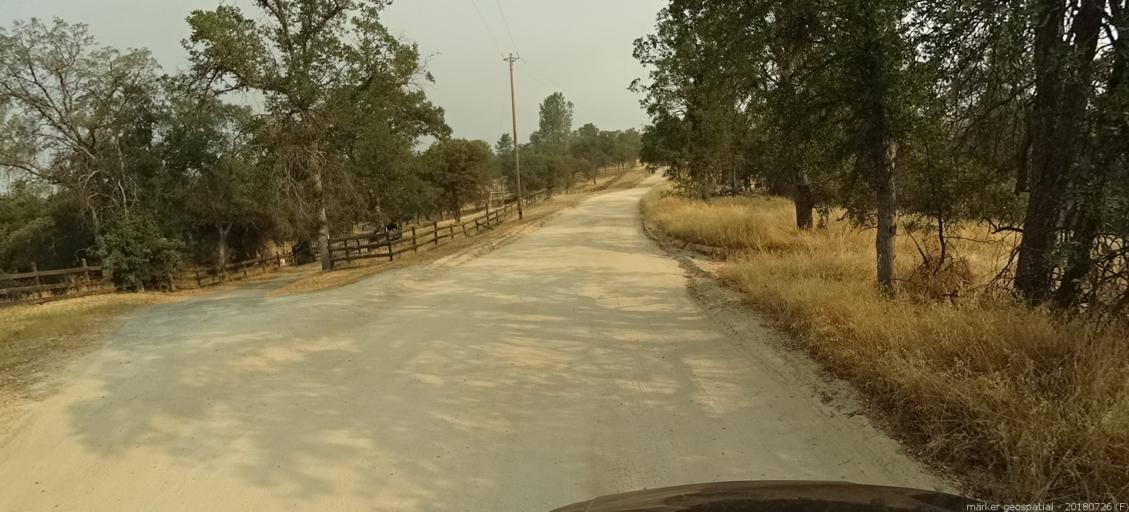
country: US
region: California
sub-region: Madera County
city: Coarsegold
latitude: 37.2214
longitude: -119.7154
